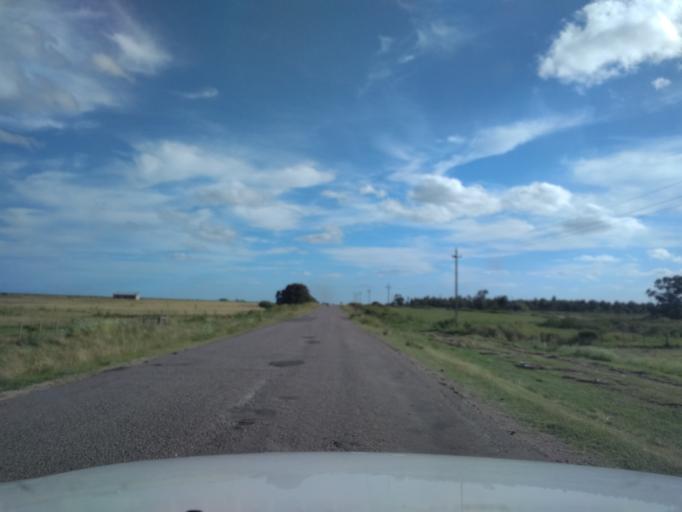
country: UY
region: Canelones
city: San Ramon
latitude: -34.2559
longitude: -55.9267
